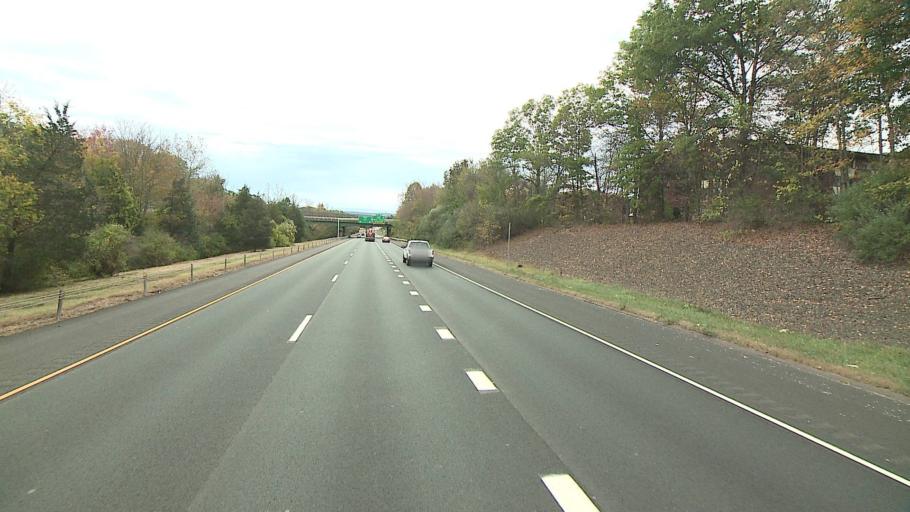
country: US
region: Connecticut
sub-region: Middlesex County
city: Cromwell
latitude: 41.6097
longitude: -72.6775
